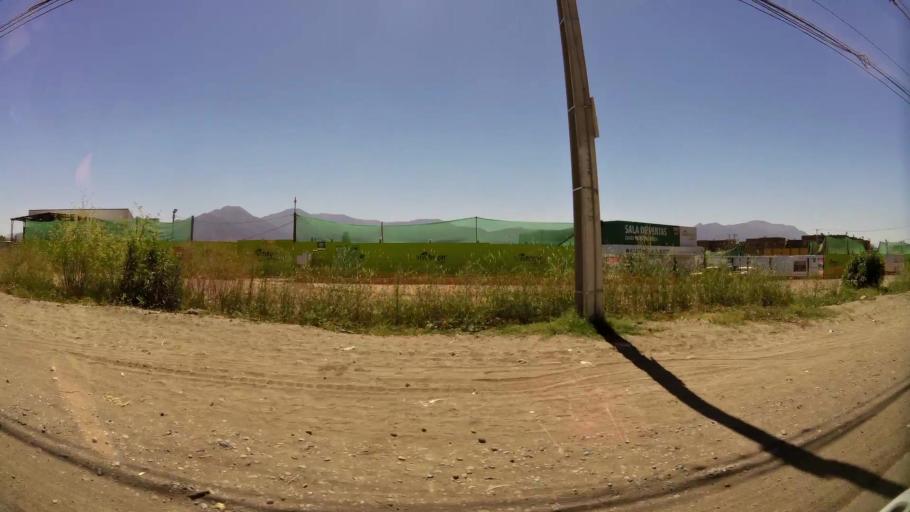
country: CL
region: O'Higgins
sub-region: Provincia de Cachapoal
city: Rancagua
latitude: -34.1742
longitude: -70.7798
